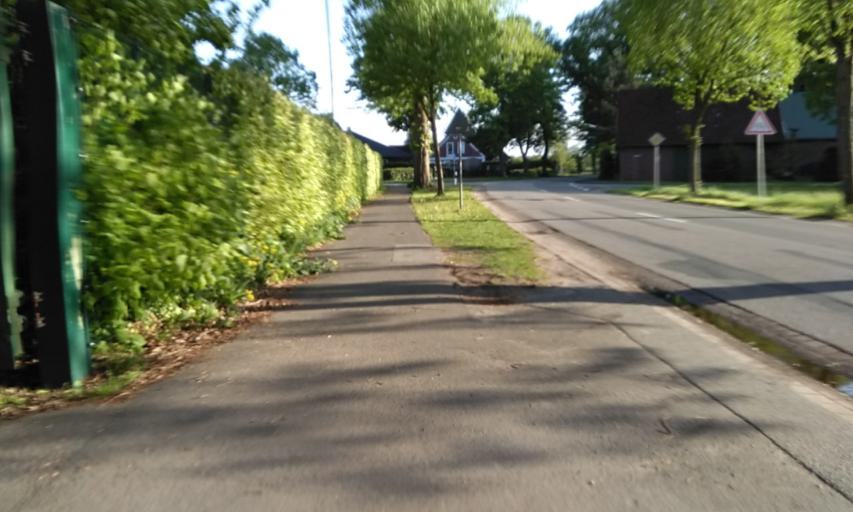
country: DE
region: Lower Saxony
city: Sauensiek
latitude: 53.4120
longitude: 9.5494
